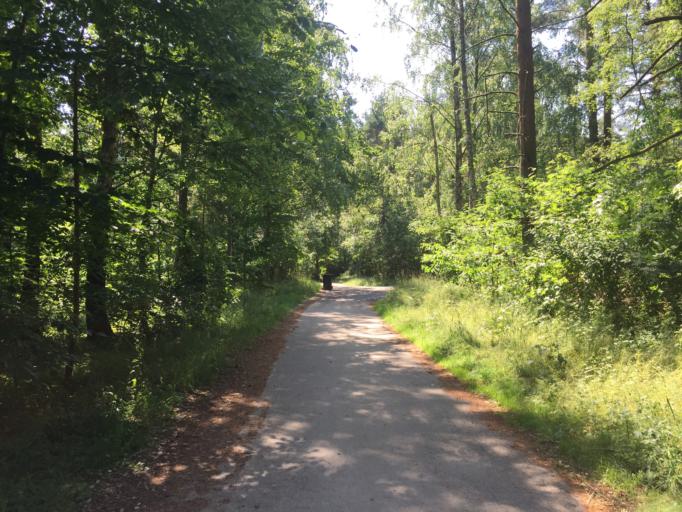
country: SE
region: Skane
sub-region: Lunds Kommun
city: Veberod
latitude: 55.6205
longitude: 13.5066
